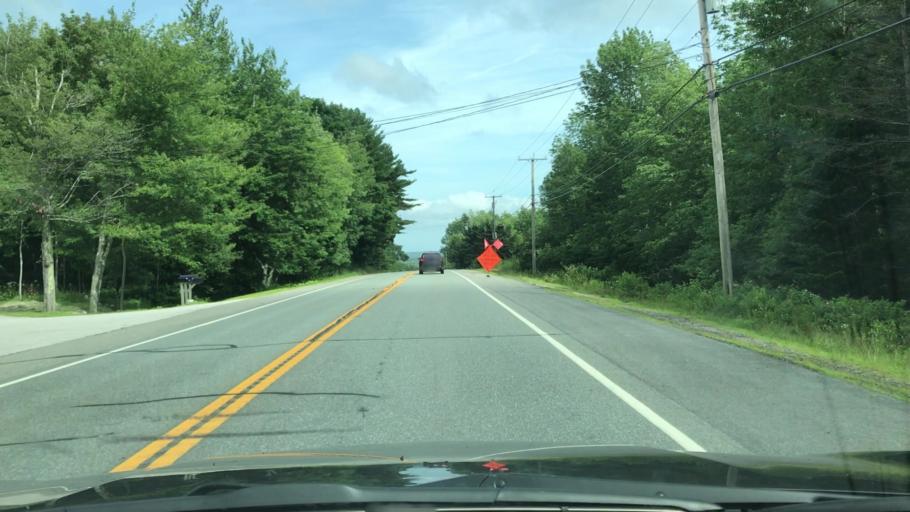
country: US
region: Maine
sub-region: Hancock County
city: Surry
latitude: 44.5437
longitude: -68.5126
